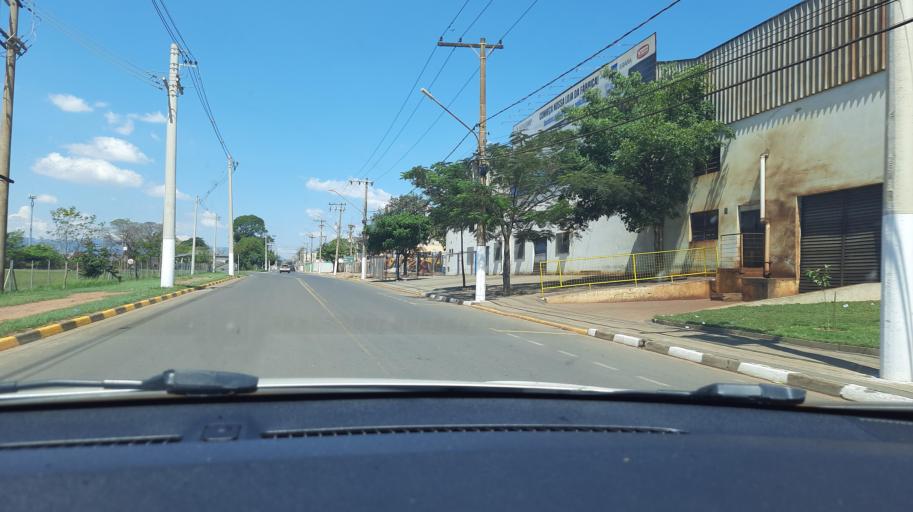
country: BR
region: Sao Paulo
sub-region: Vargem Grande Do Sul
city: Vargem Grande do Sul
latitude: -21.8413
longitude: -46.9079
